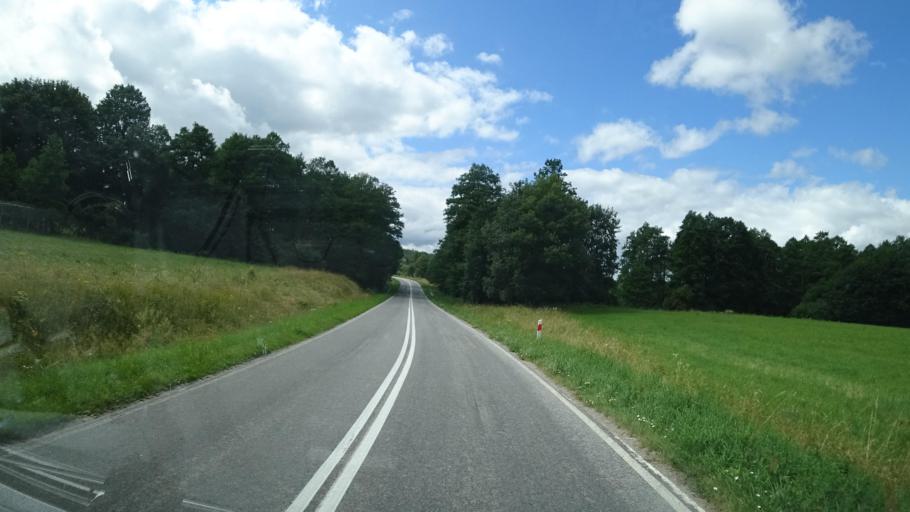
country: PL
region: Warmian-Masurian Voivodeship
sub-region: Powiat goldapski
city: Banie Mazurskie
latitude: 54.2146
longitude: 22.1631
